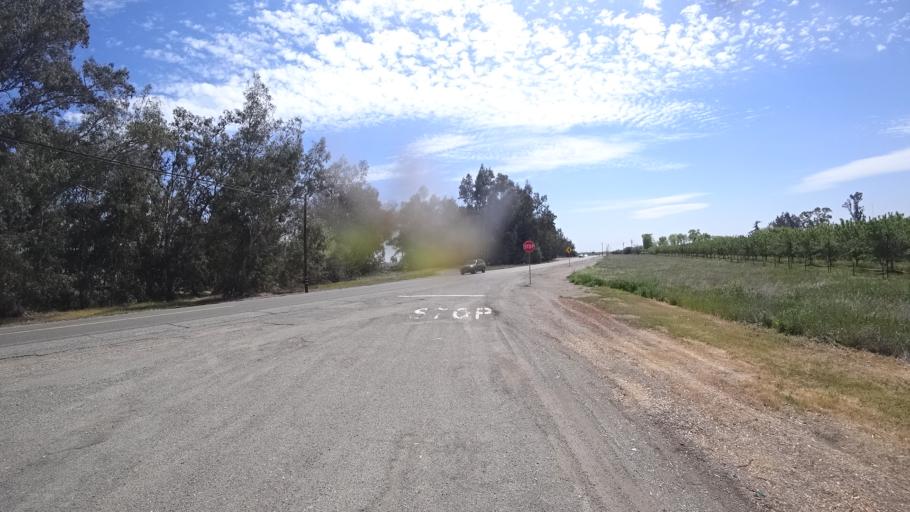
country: US
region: California
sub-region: Glenn County
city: Willows
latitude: 39.5856
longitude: -122.1948
